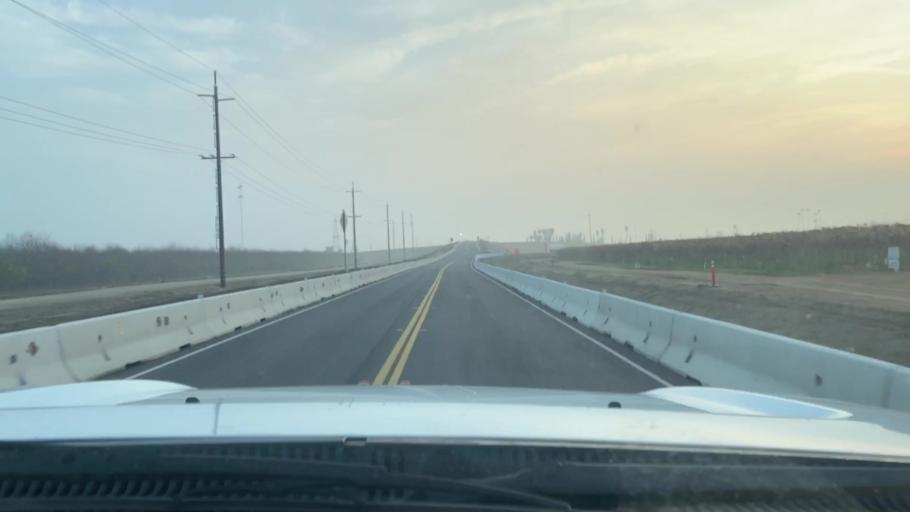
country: US
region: California
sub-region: Kern County
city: McFarland
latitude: 35.6019
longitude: -119.2187
